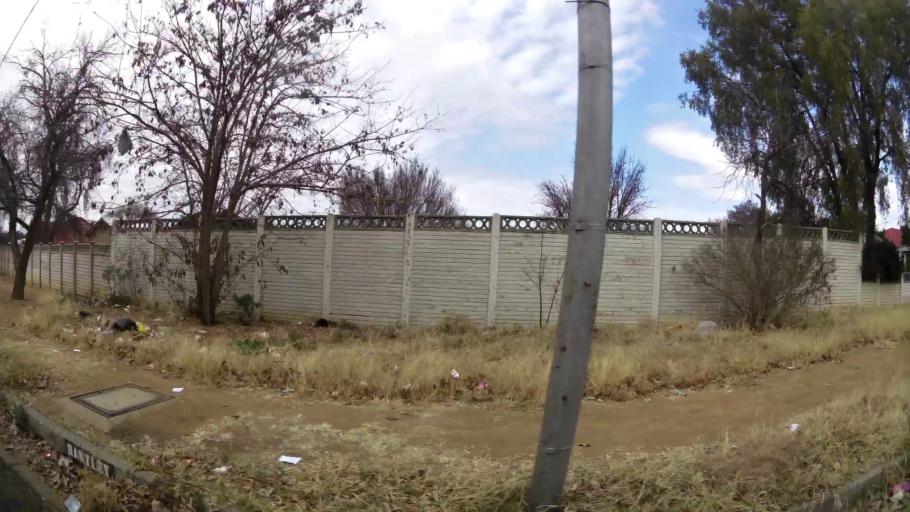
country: ZA
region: Orange Free State
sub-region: Fezile Dabi District Municipality
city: Kroonstad
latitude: -27.6345
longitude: 27.2262
